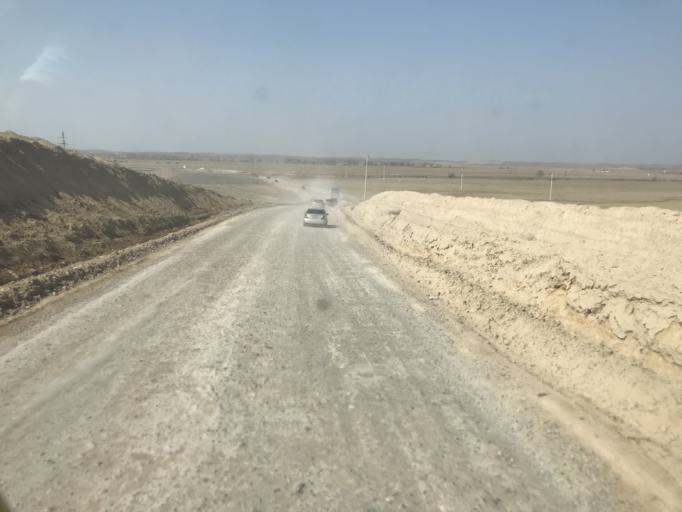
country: KG
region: Chuy
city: Bystrovka
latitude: 43.3221
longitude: 76.0430
